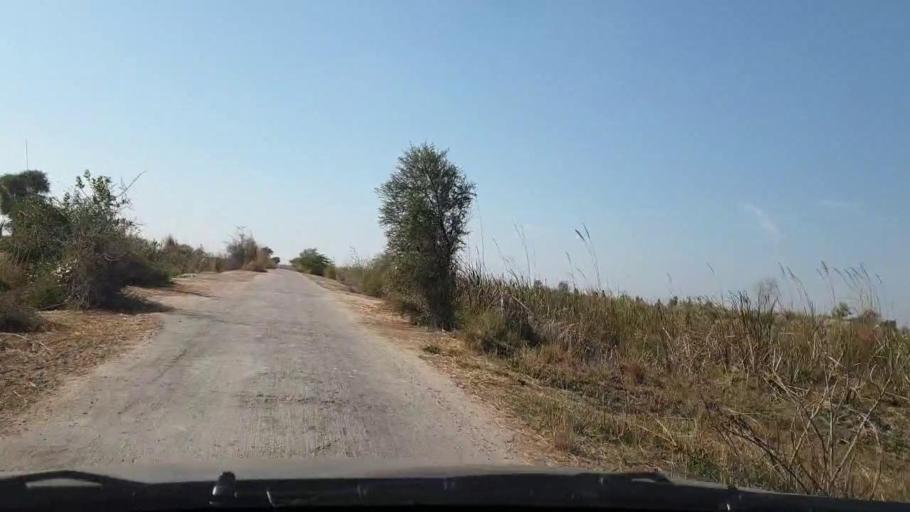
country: PK
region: Sindh
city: Khadro
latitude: 26.2674
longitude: 68.8088
